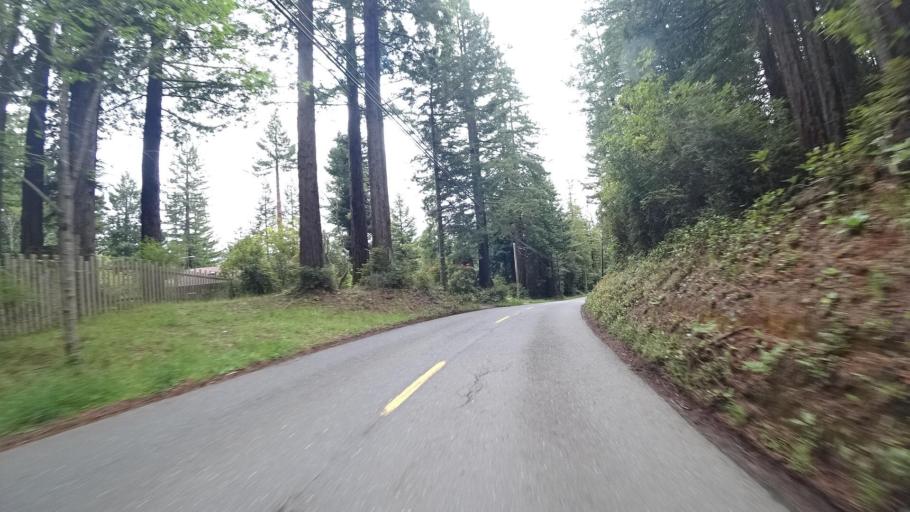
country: US
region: California
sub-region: Humboldt County
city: Bayside
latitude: 40.7917
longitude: -124.0558
